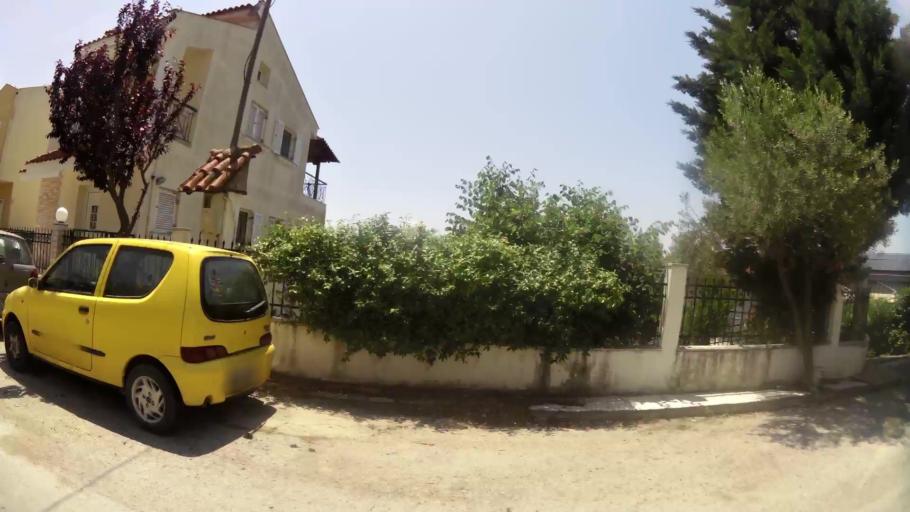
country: GR
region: Central Macedonia
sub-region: Nomos Thessalonikis
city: Trilofos
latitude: 40.4740
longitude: 22.9693
